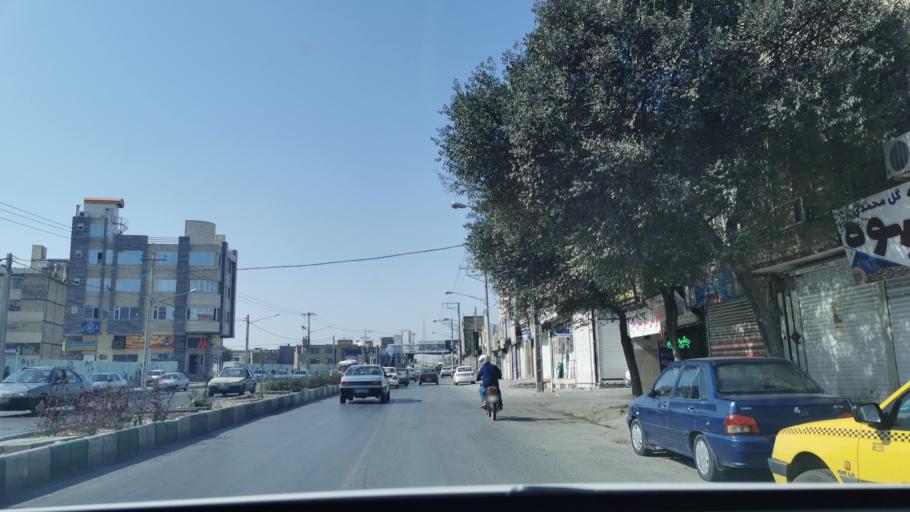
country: IR
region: Razavi Khorasan
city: Mashhad
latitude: 36.3240
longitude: 59.6415
